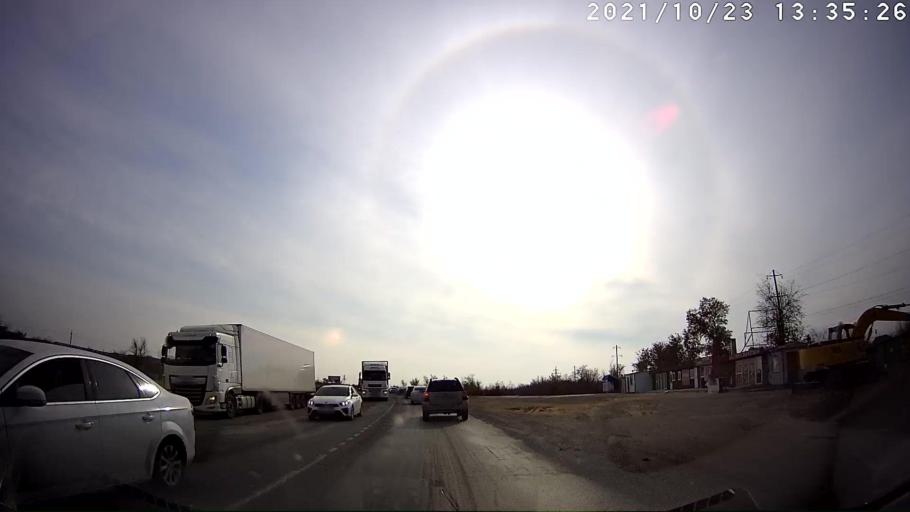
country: RU
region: Volgograd
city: Vodstroy
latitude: 48.8573
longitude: 44.5620
